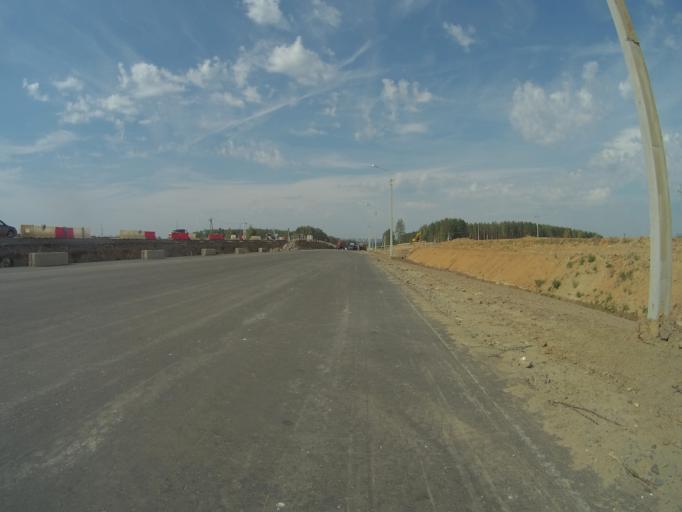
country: RU
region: Vladimir
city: Kommunar
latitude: 56.0714
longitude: 40.4936
